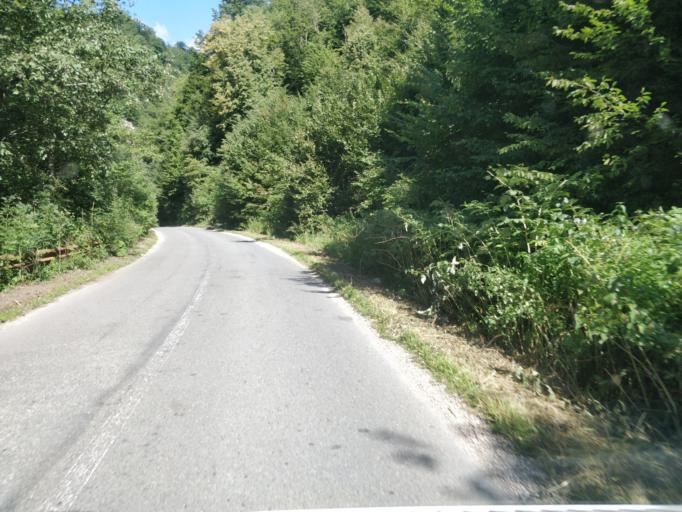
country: RO
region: Cluj
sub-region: Comuna Sacueu
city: Sacuieu
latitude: 46.8411
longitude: 22.8626
